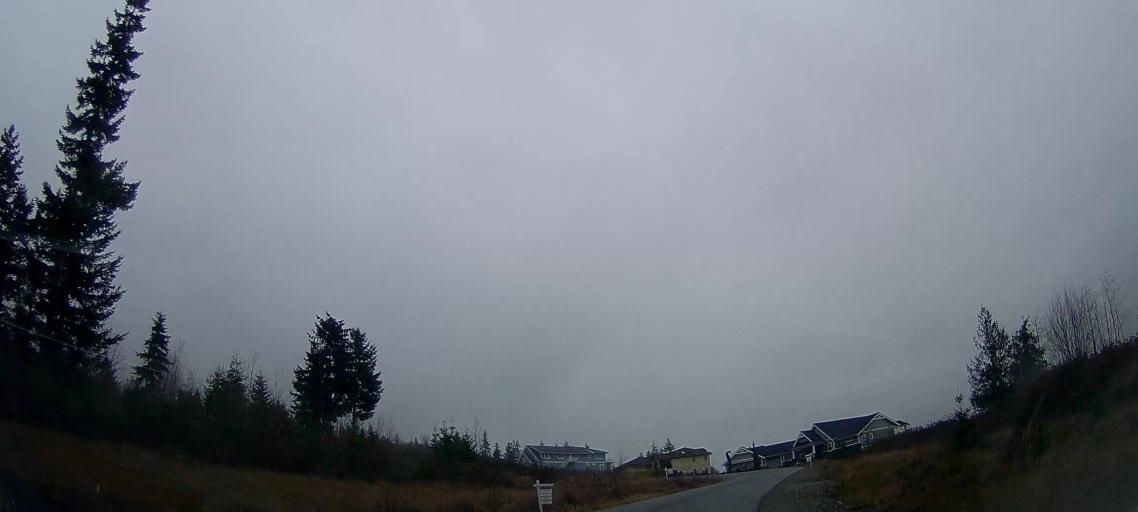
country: US
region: Washington
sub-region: Skagit County
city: Mount Vernon
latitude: 48.3700
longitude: -122.3057
